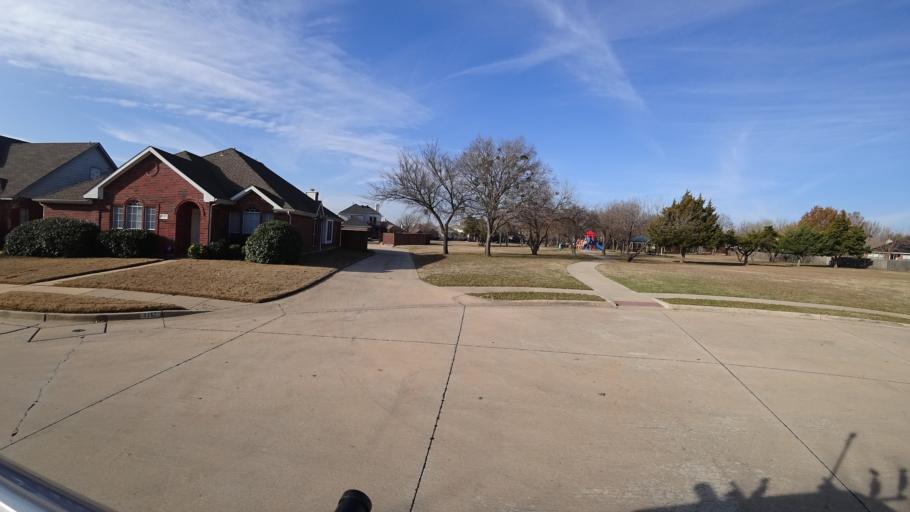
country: US
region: Texas
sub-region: Denton County
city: Lewisville
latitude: 33.0600
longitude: -97.0232
